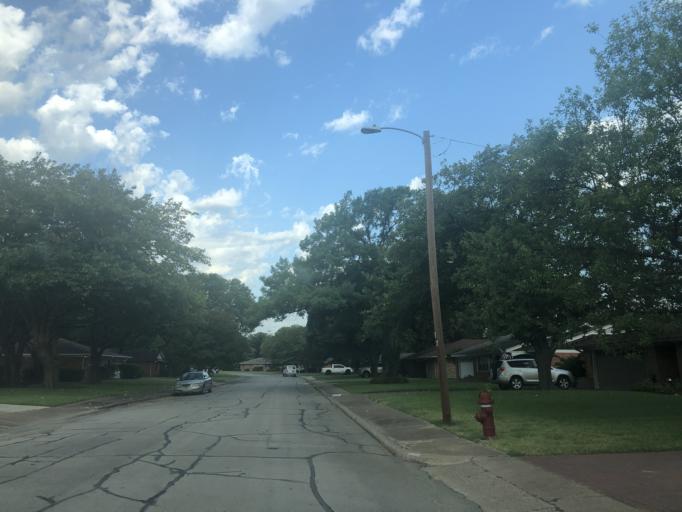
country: US
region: Texas
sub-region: Dallas County
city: Grand Prairie
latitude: 32.7626
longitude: -97.0144
